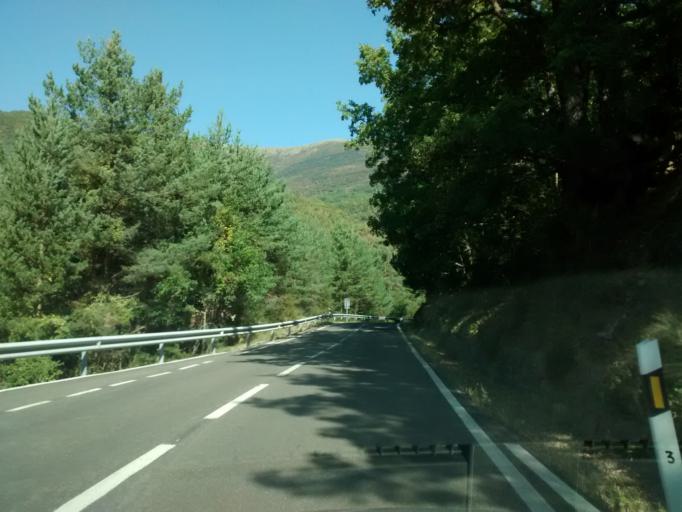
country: ES
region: Aragon
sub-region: Provincia de Huesca
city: Fiscal
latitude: 42.5330
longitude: -0.1402
